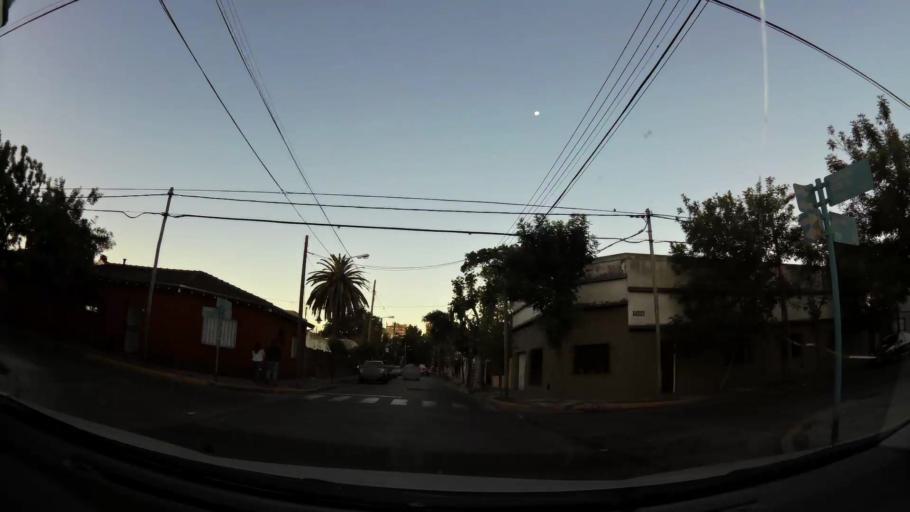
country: AR
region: Buenos Aires
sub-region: Partido de Tigre
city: Tigre
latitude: -34.4421
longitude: -58.5635
